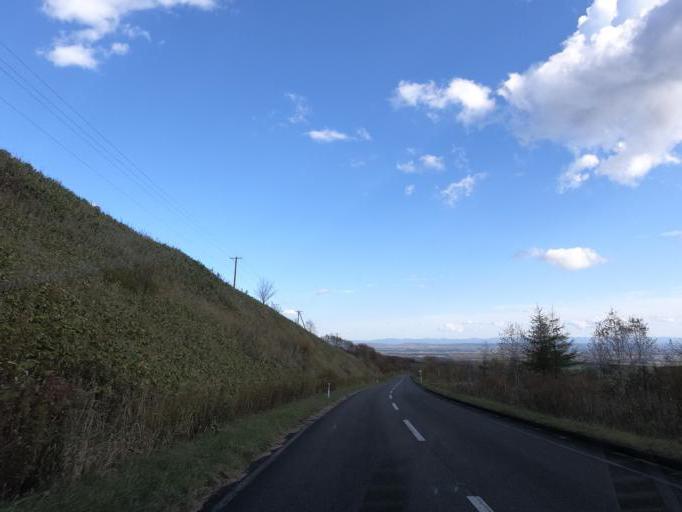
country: JP
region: Hokkaido
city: Otofuke
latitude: 43.2931
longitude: 143.1947
